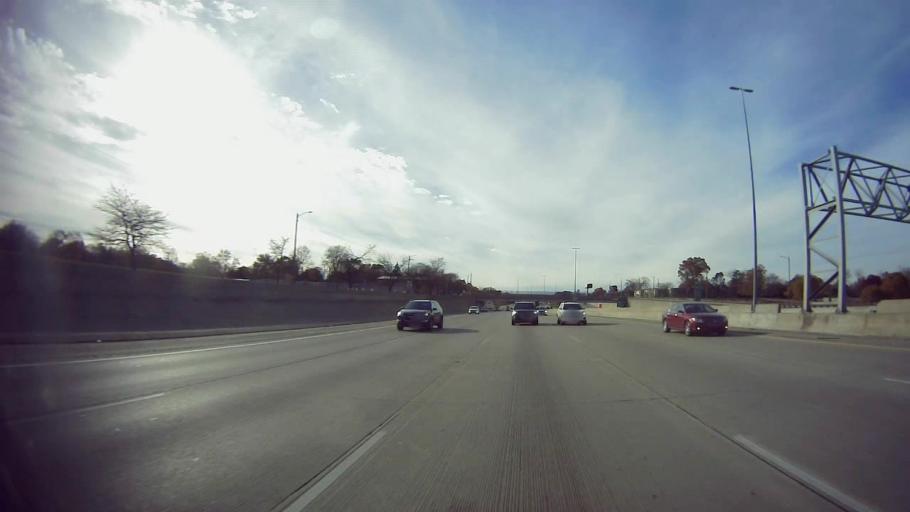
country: US
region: Michigan
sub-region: Wayne County
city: Redford
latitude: 42.3855
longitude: -83.2686
